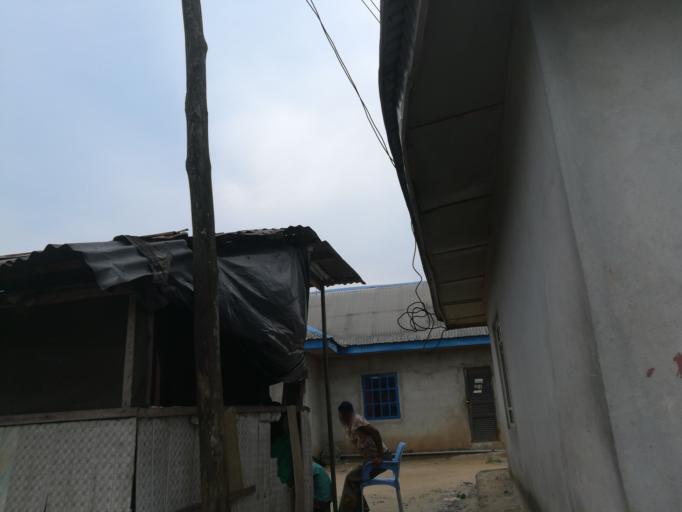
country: NG
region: Rivers
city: Okrika
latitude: 4.7860
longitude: 7.1242
